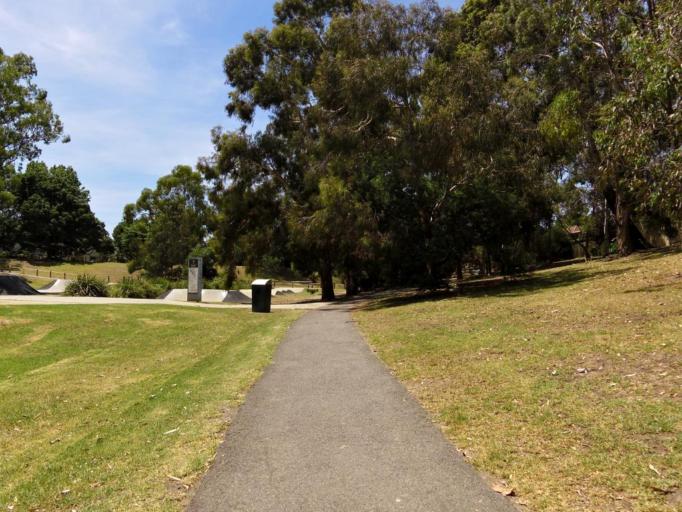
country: AU
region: Victoria
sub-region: Boroondara
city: Ashburton
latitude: -37.8567
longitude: 145.0745
